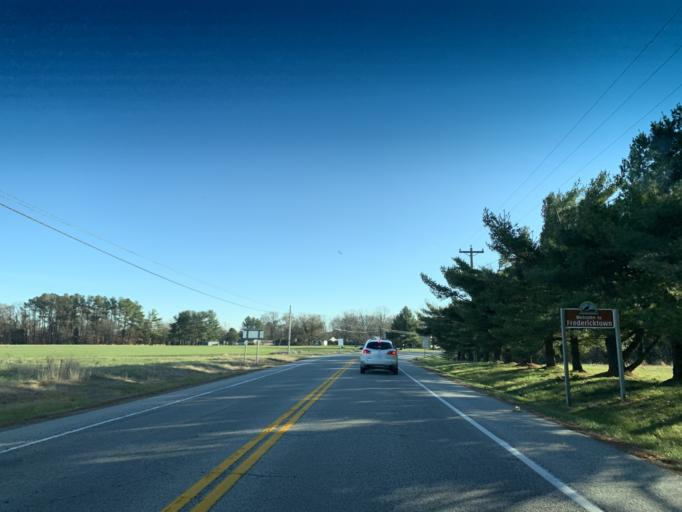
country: US
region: Delaware
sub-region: New Castle County
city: Middletown
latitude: 39.3712
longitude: -75.8832
